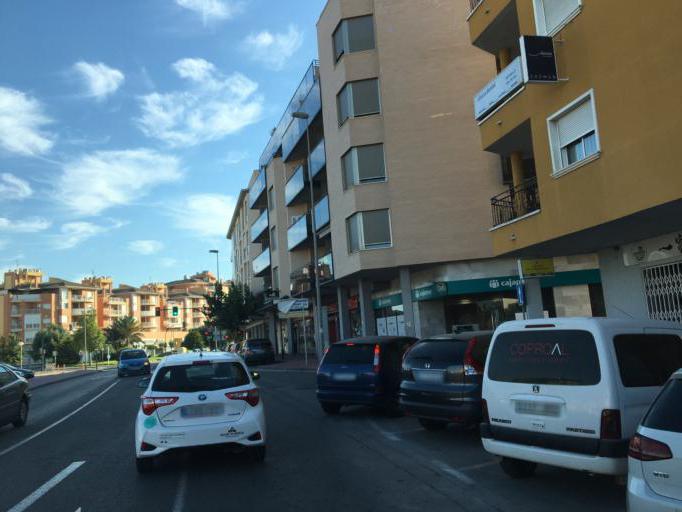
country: ES
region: Murcia
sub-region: Murcia
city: Murcia
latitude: 38.0218
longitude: -1.1360
